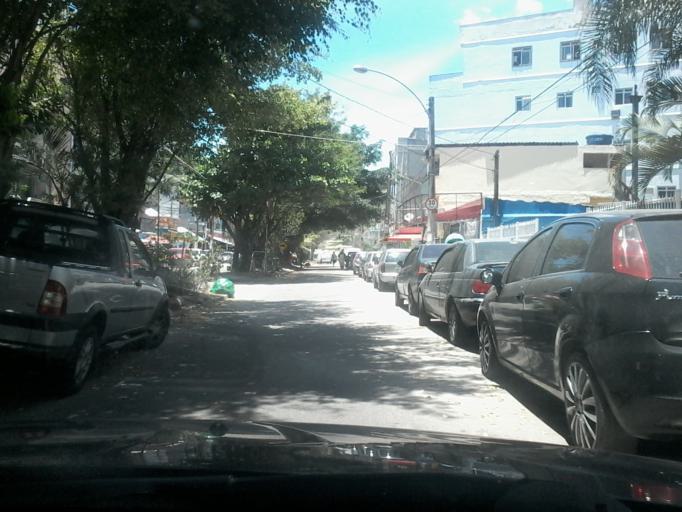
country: BR
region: Rio de Janeiro
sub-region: Nilopolis
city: Nilopolis
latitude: -23.0295
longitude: -43.4727
